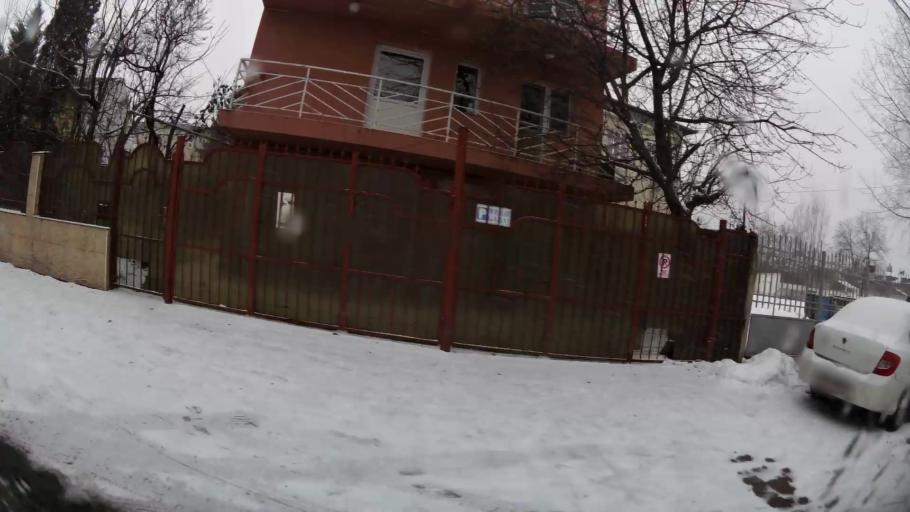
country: RO
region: Dambovita
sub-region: Municipiul Targoviste
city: Targoviste
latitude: 44.9293
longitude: 25.4648
